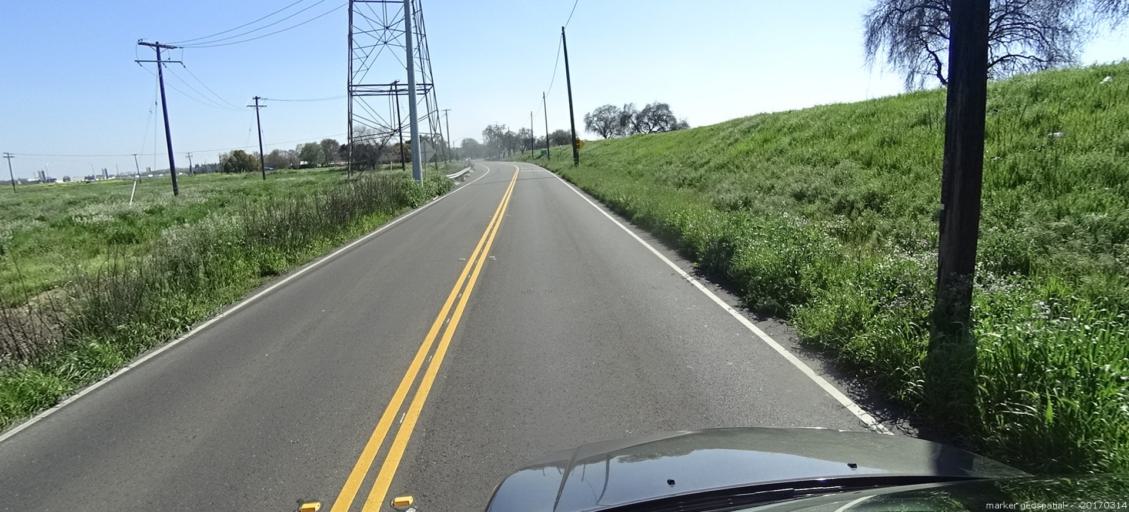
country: US
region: California
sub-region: Sacramento County
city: Parkway
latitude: 38.4681
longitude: -121.5033
